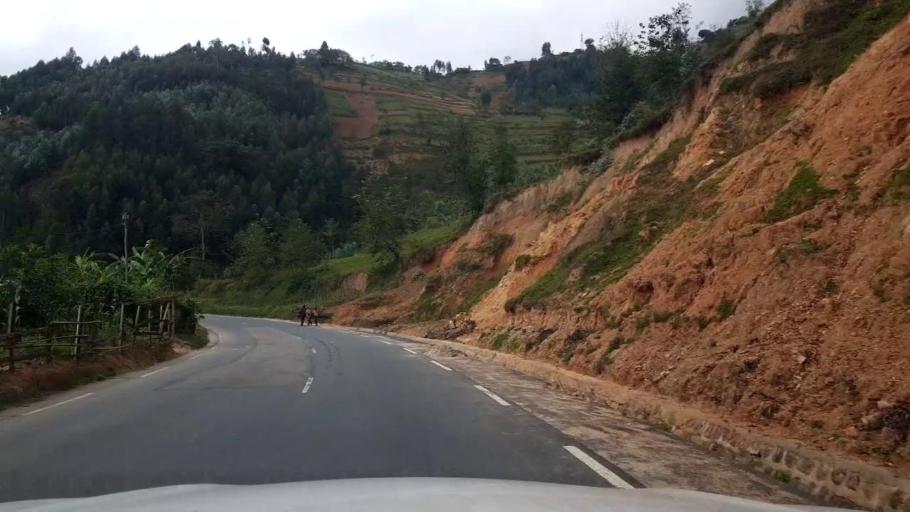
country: RW
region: Northern Province
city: Musanze
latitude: -1.6933
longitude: 29.5566
